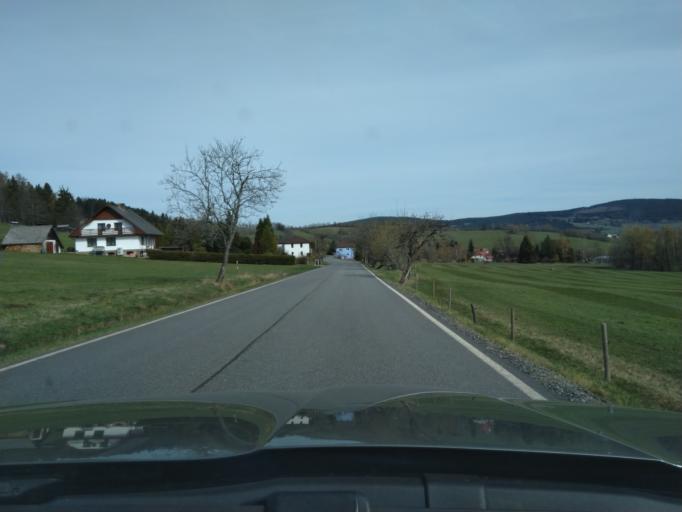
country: CZ
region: Jihocesky
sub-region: Okres Prachatice
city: Stachy
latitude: 49.0974
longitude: 13.6474
